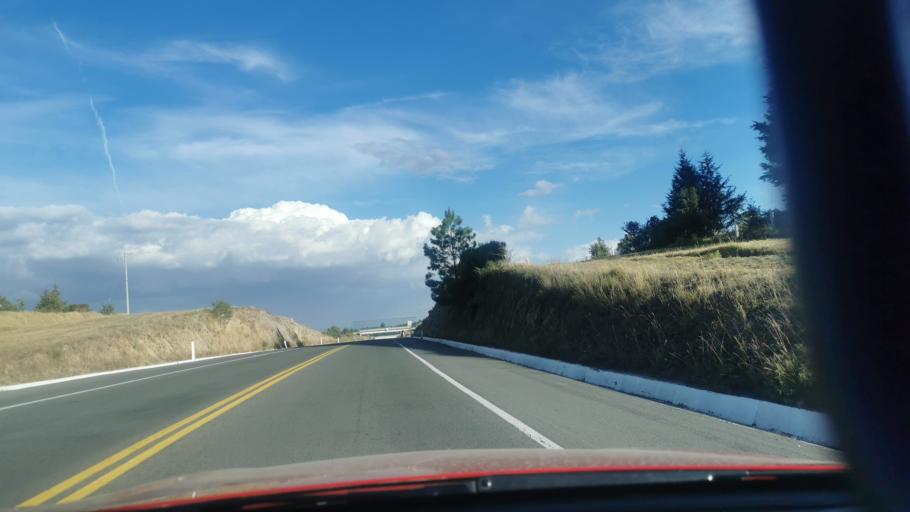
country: MX
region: Mexico
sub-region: Villa Victoria
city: Colonia Doctor Gustavo Baz
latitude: 19.3774
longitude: -99.8802
